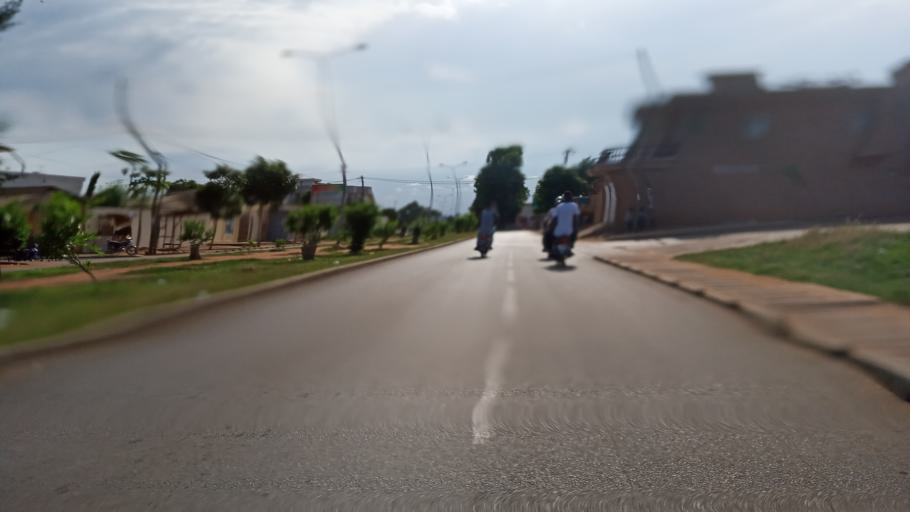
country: TG
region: Maritime
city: Lome
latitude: 6.1874
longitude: 1.2600
